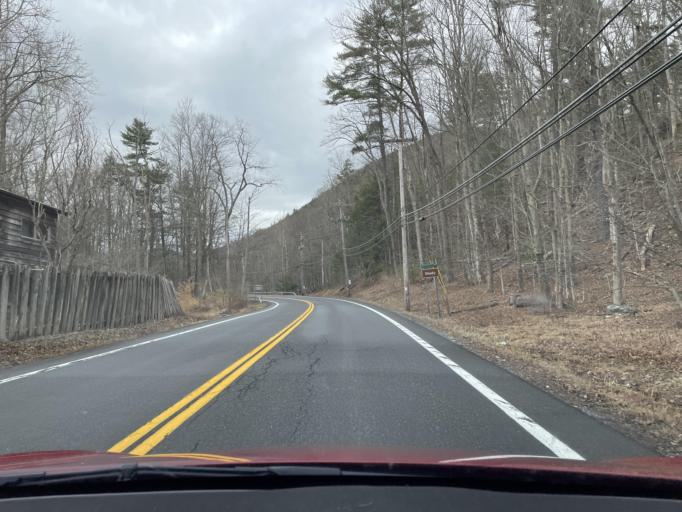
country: US
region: New York
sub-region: Ulster County
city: Woodstock
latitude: 42.0547
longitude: -74.1587
